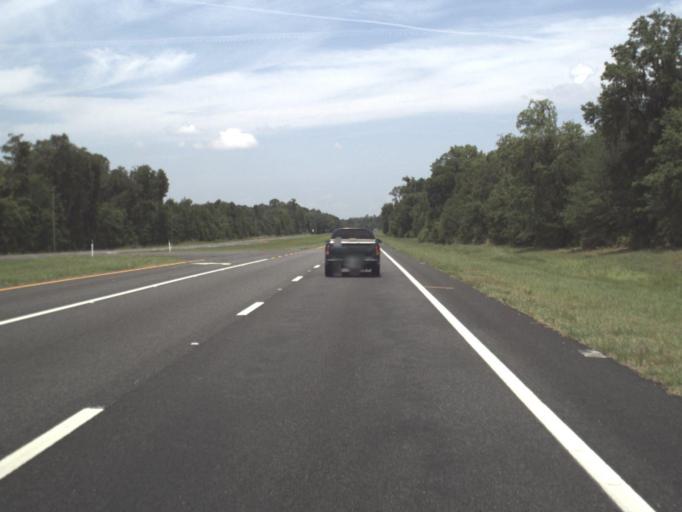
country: US
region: Florida
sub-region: Alachua County
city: Gainesville
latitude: 29.6086
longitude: -82.2340
